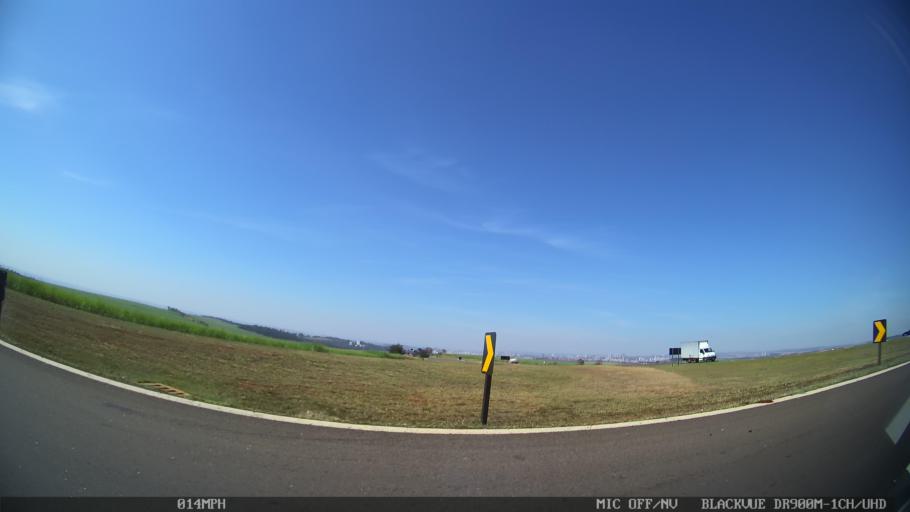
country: BR
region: Sao Paulo
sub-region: Ribeirao Preto
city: Ribeirao Preto
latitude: -21.1660
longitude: -47.8986
